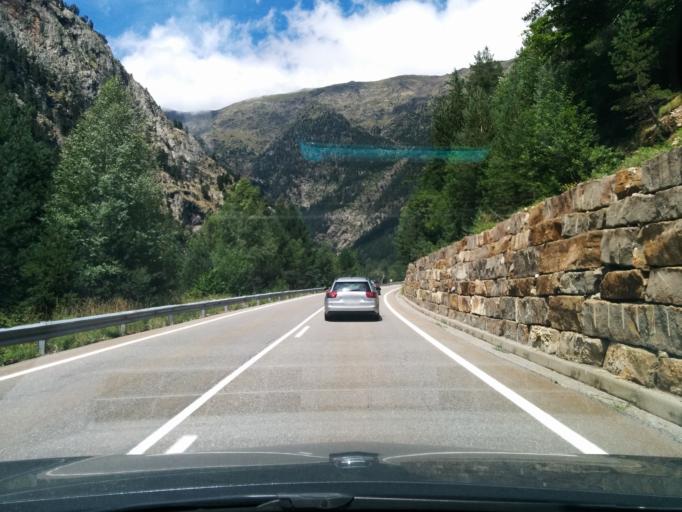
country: ES
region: Aragon
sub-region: Provincia de Huesca
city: Bielsa
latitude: 42.7067
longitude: 0.2017
